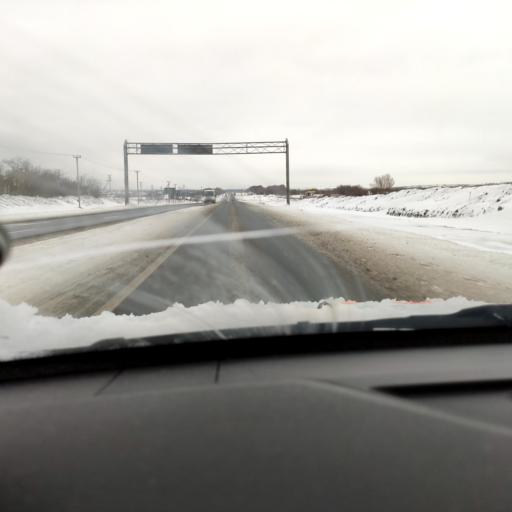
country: RU
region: Samara
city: Novosemeykino
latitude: 53.4212
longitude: 50.3520
